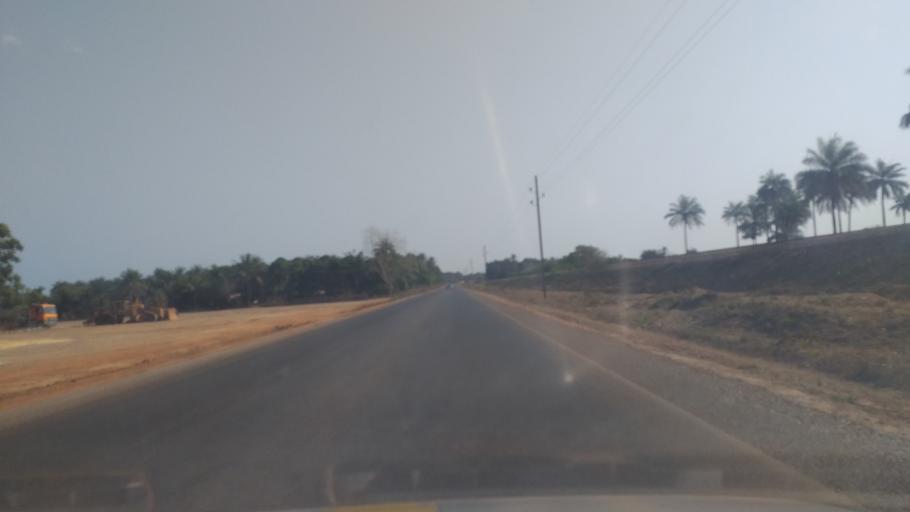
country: GN
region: Boke
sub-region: Boke Prefecture
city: Kamsar
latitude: 10.7293
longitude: -14.5179
